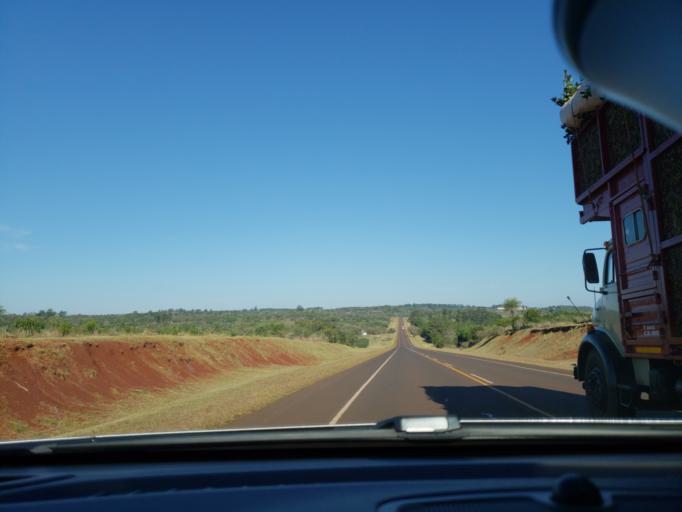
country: AR
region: Misiones
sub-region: Departamento de Apostoles
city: San Jose
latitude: -27.8404
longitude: -55.7673
